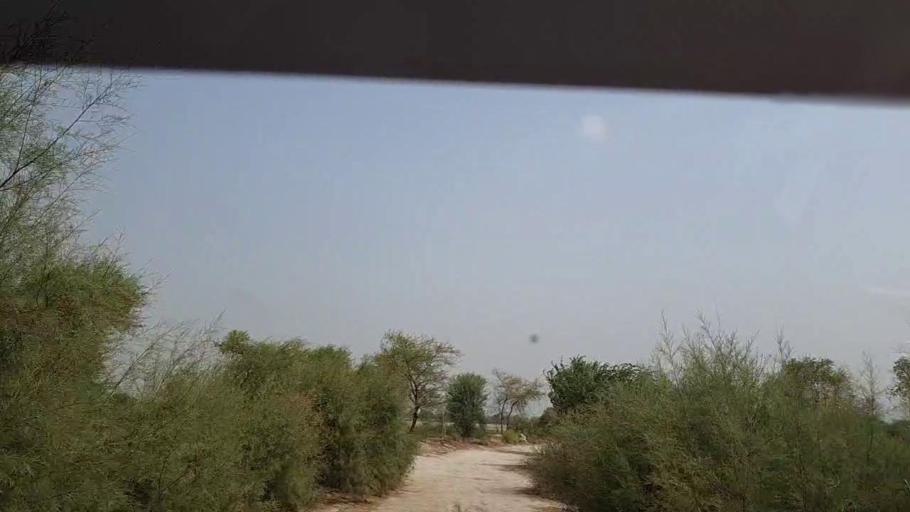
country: PK
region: Sindh
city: Khairpur Nathan Shah
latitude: 27.0287
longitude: 67.6754
